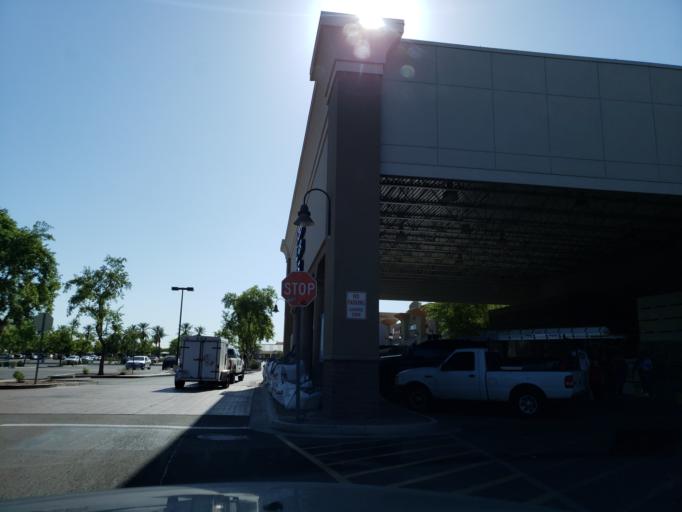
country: US
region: Arizona
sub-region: Maricopa County
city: Glendale
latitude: 33.5516
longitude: -112.1837
